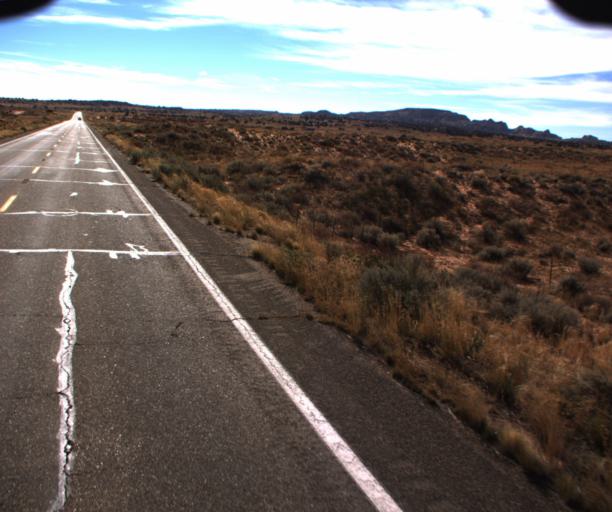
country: US
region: Arizona
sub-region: Coconino County
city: Kaibito
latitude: 36.5903
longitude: -111.1568
